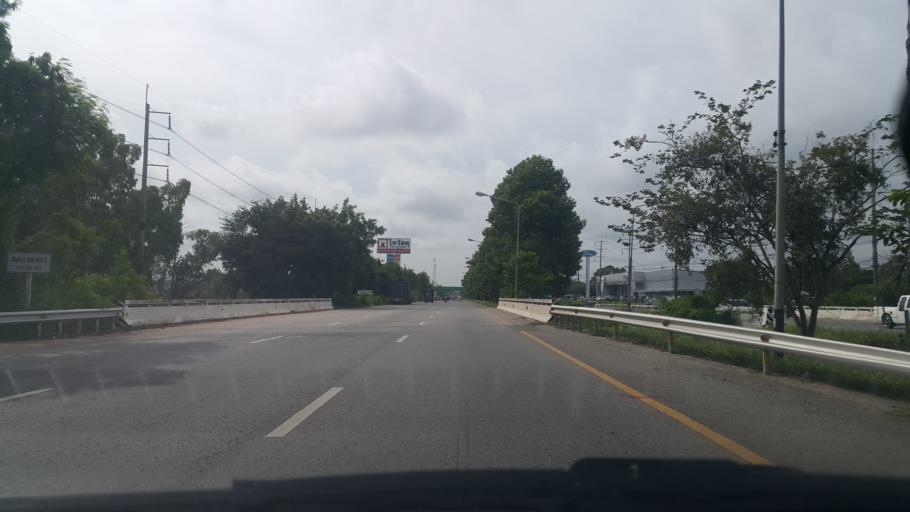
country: TH
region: Rayong
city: Rayong
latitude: 12.6673
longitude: 101.3073
